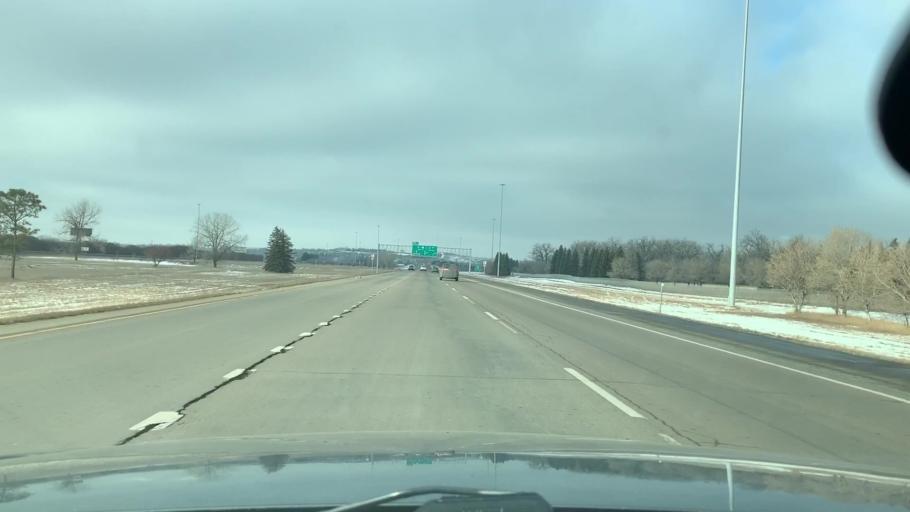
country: US
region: North Dakota
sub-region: Morton County
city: Mandan
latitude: 46.8241
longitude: -100.8467
